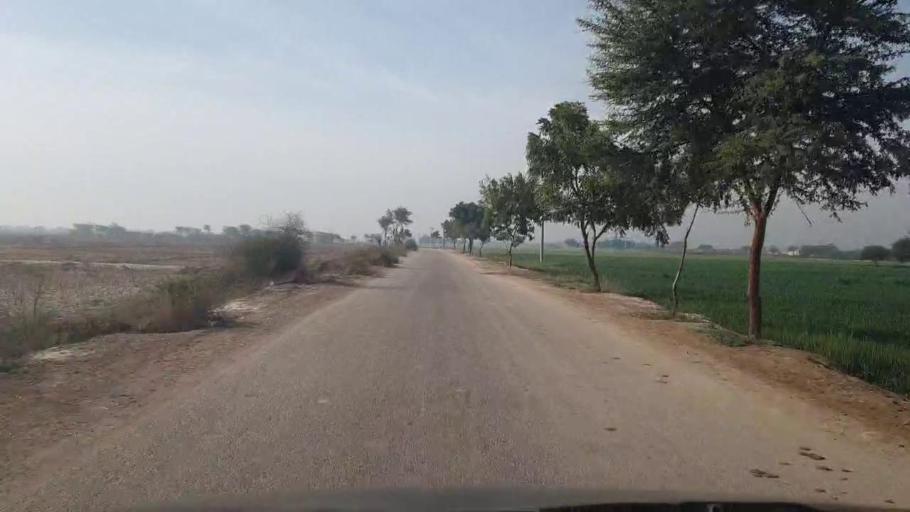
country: PK
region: Sindh
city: Umarkot
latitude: 25.3522
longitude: 69.6985
